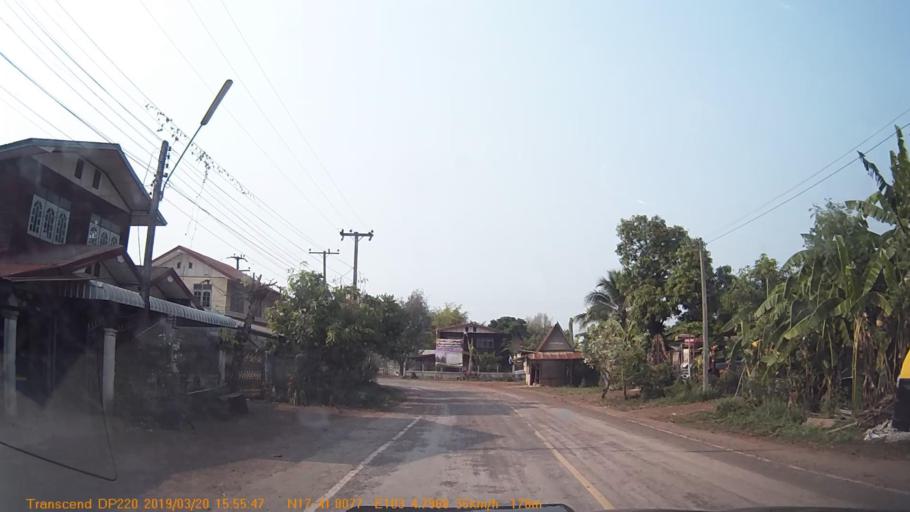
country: TH
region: Changwat Udon Thani
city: Phibun Rak
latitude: 17.6836
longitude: 103.0799
